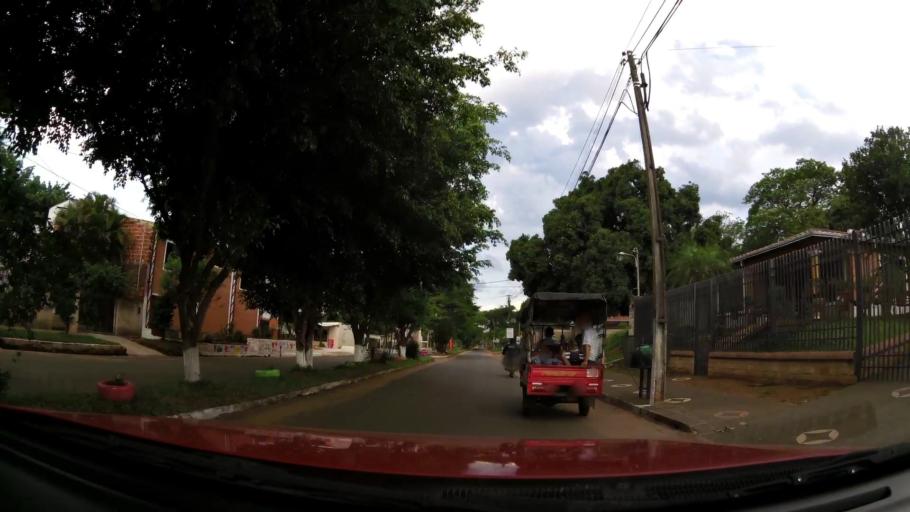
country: PY
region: Central
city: Nemby
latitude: -25.3725
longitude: -57.5483
